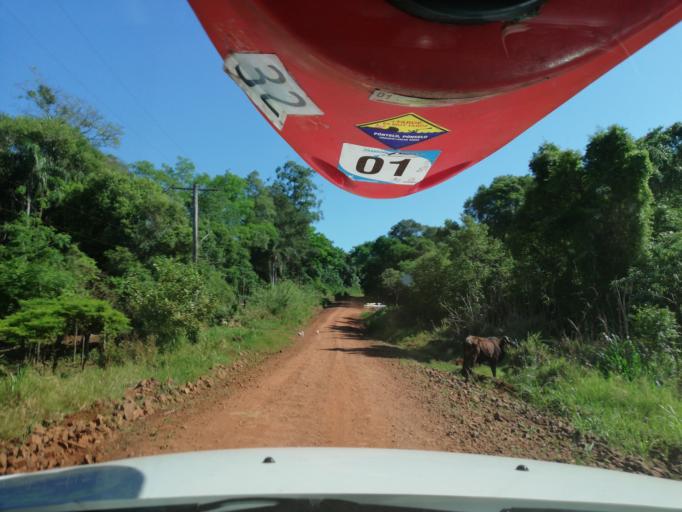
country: AR
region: Misiones
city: Puerto Leoni
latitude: -26.9699
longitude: -55.1646
